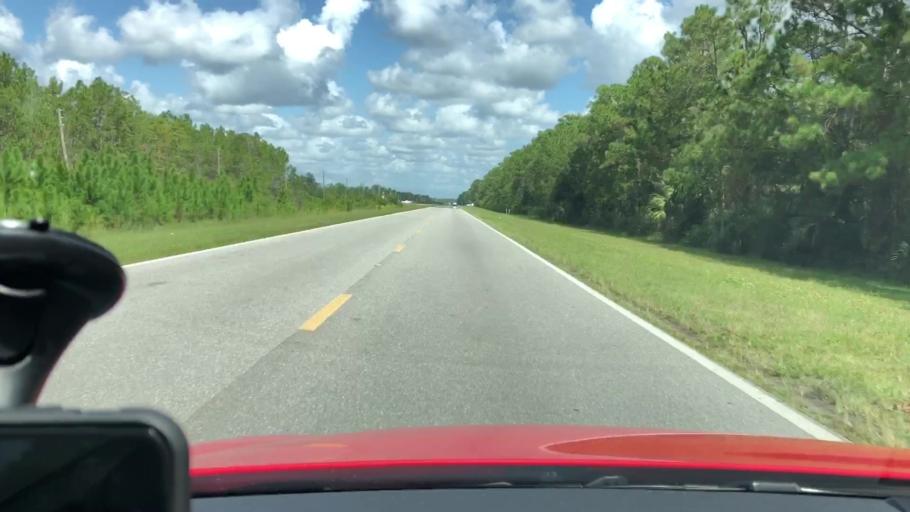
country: US
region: Florida
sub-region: Volusia County
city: Daytona Beach
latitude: 29.1861
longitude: -81.1197
